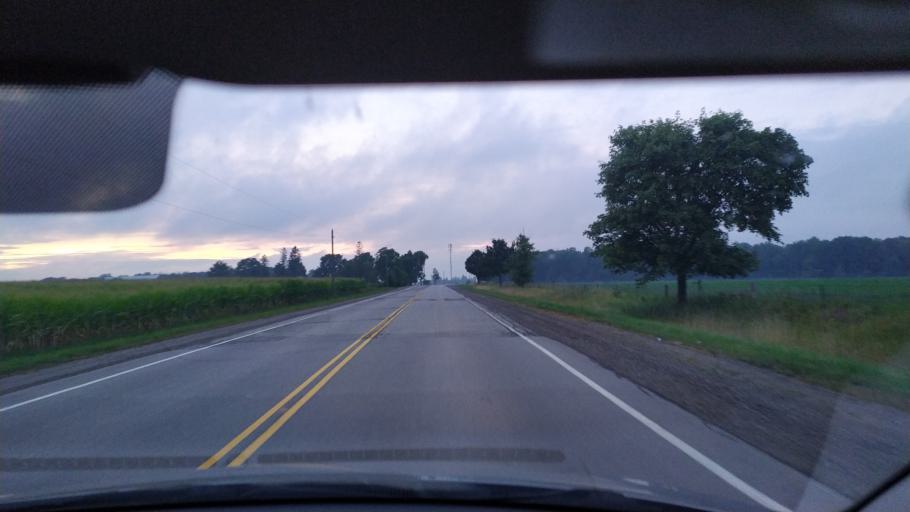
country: CA
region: Ontario
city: Kitchener
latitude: 43.3558
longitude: -80.7016
